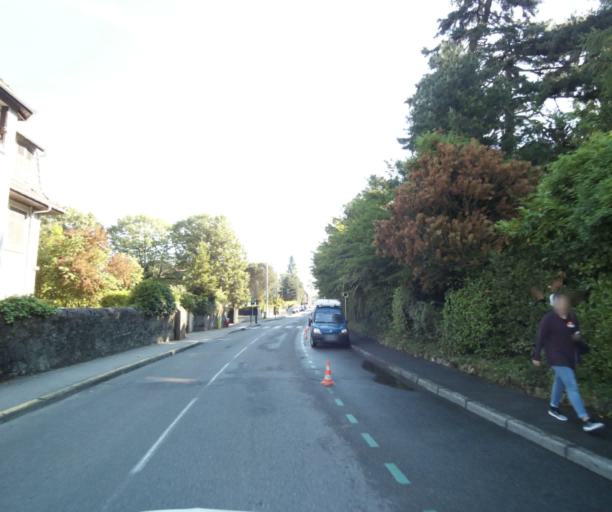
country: FR
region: Rhone-Alpes
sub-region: Departement de la Haute-Savoie
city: Thonon-les-Bains
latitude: 46.3767
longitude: 6.4825
